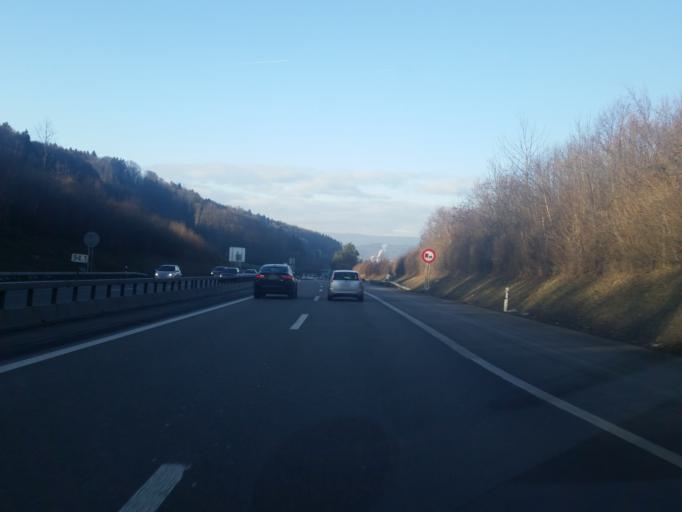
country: CH
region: Zurich
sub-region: Bezirk Dietikon
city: Urdorf / Oberurdorf
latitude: 47.3762
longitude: 8.4190
